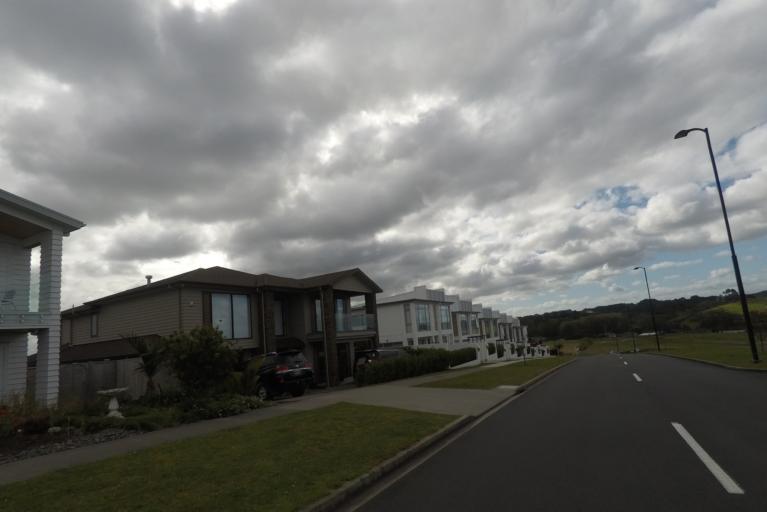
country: NZ
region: Auckland
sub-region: Auckland
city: Rothesay Bay
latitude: -36.6037
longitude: 174.6705
